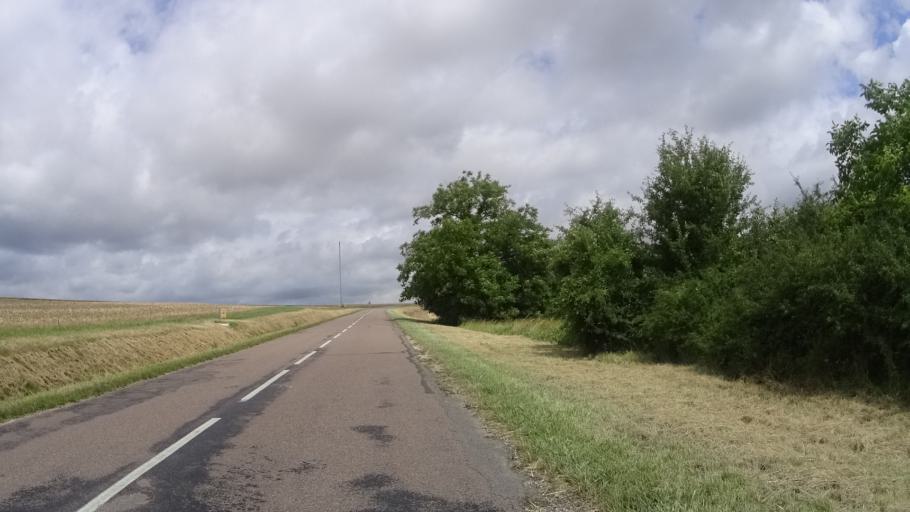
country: FR
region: Champagne-Ardenne
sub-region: Departement de l'Aube
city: Ervy-le-Chatel
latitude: 48.1068
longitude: 3.9509
